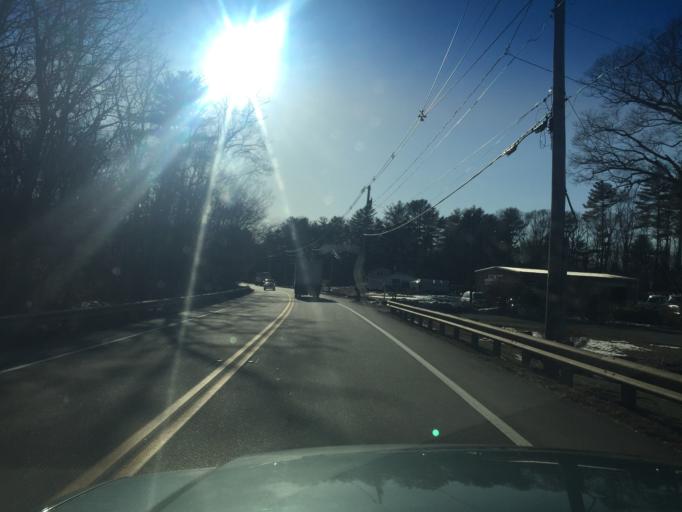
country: US
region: Massachusetts
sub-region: Worcester County
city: Mendon
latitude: 42.0930
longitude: -71.5904
